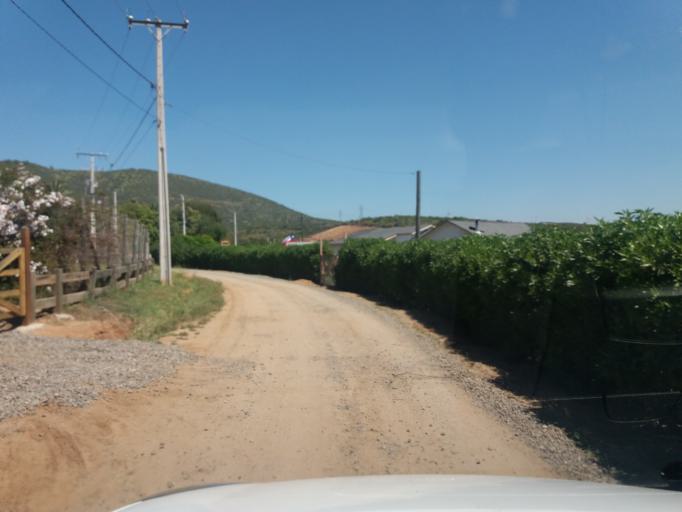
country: CL
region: Valparaiso
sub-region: Provincia de Quillota
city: Quillota
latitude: -32.9479
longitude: -71.2706
